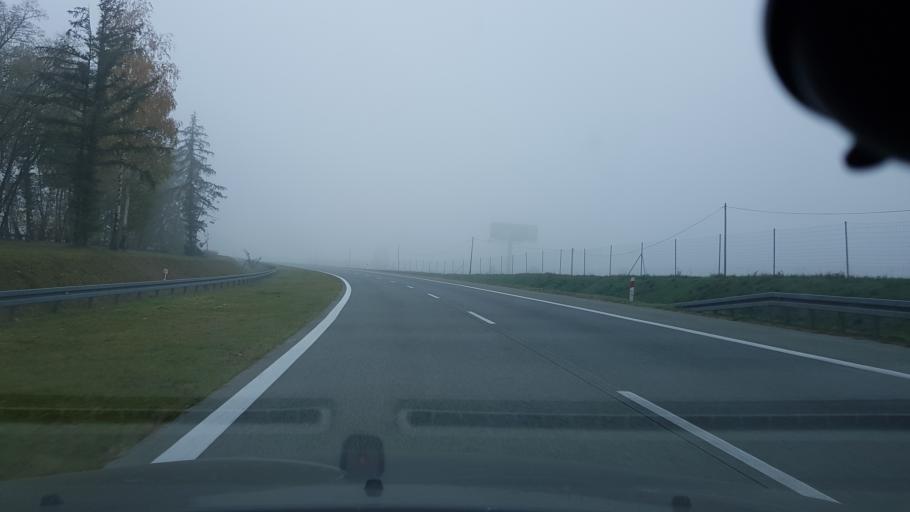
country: PL
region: Lodz Voivodeship
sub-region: Powiat skierniewicki
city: Kowiesy
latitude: 51.8769
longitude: 20.3893
